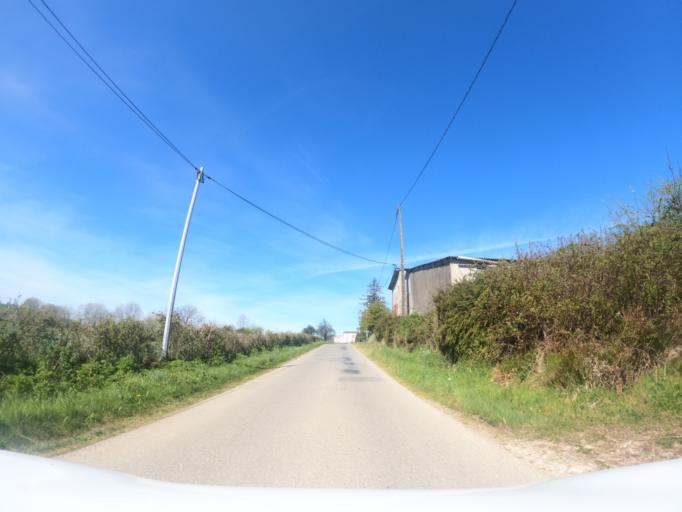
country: FR
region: Pays de la Loire
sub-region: Departement de la Vendee
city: Saint-Pierre-du-Chemin
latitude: 46.6875
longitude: -0.7063
